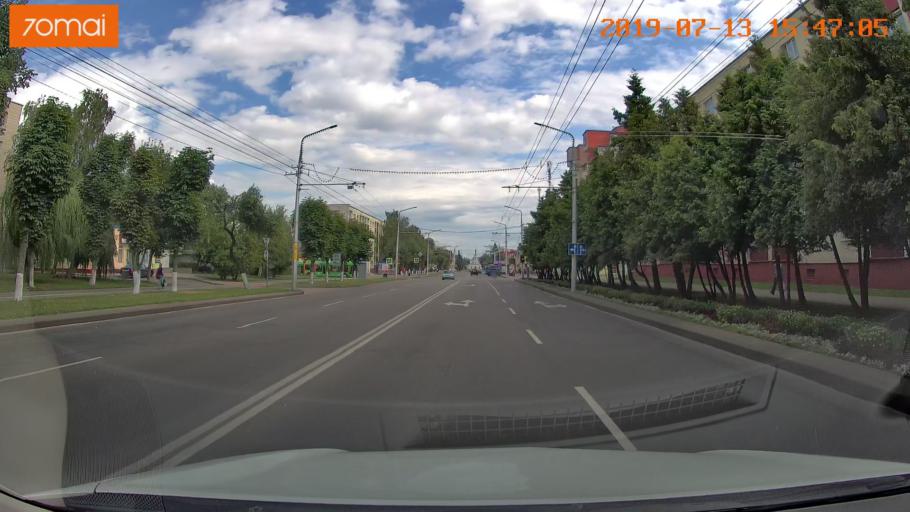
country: BY
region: Mogilev
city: Babruysk
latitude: 53.1495
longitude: 29.2284
